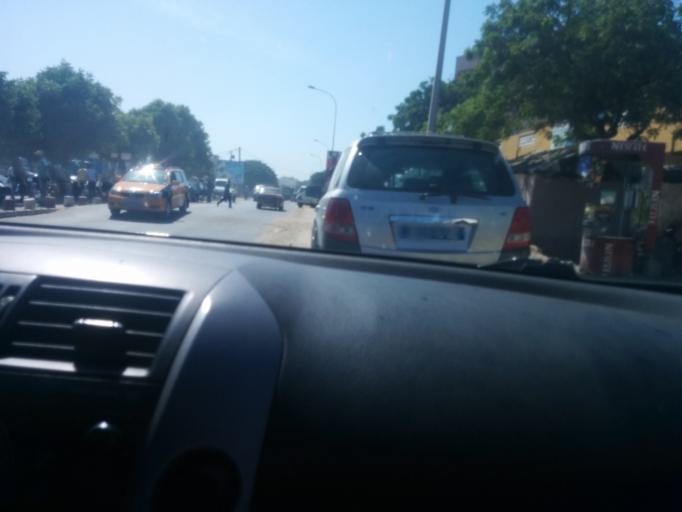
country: SN
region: Dakar
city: Grand Dakar
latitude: 14.7318
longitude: -17.4463
